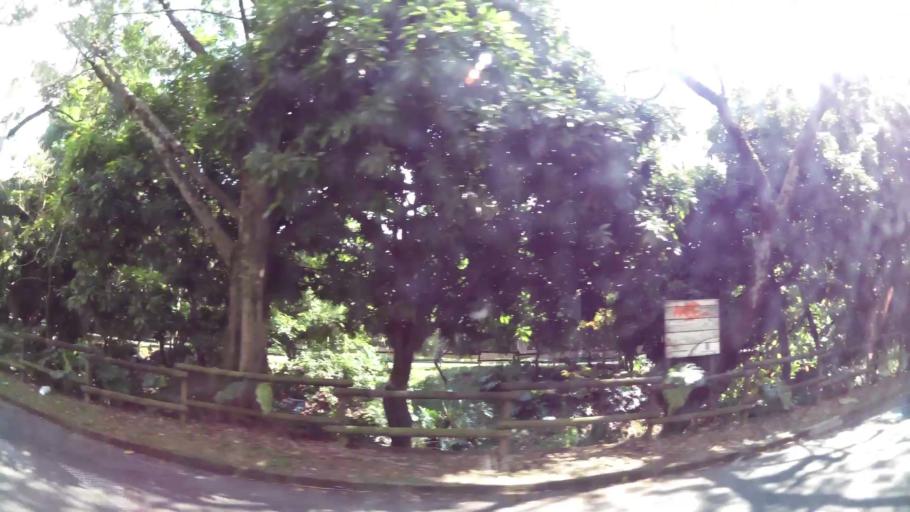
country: CO
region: Antioquia
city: Itagui
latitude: 6.2170
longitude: -75.5963
